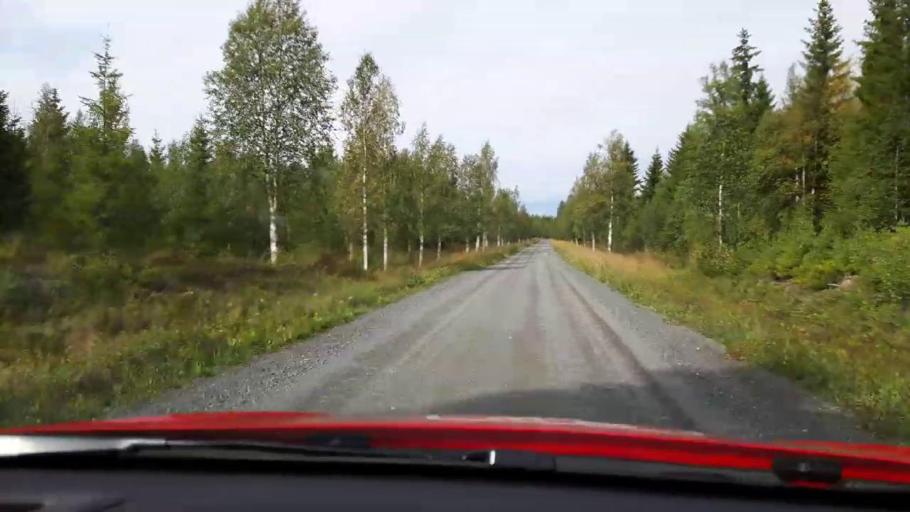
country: SE
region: Jaemtland
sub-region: Krokoms Kommun
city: Valla
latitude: 63.2611
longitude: 13.8009
